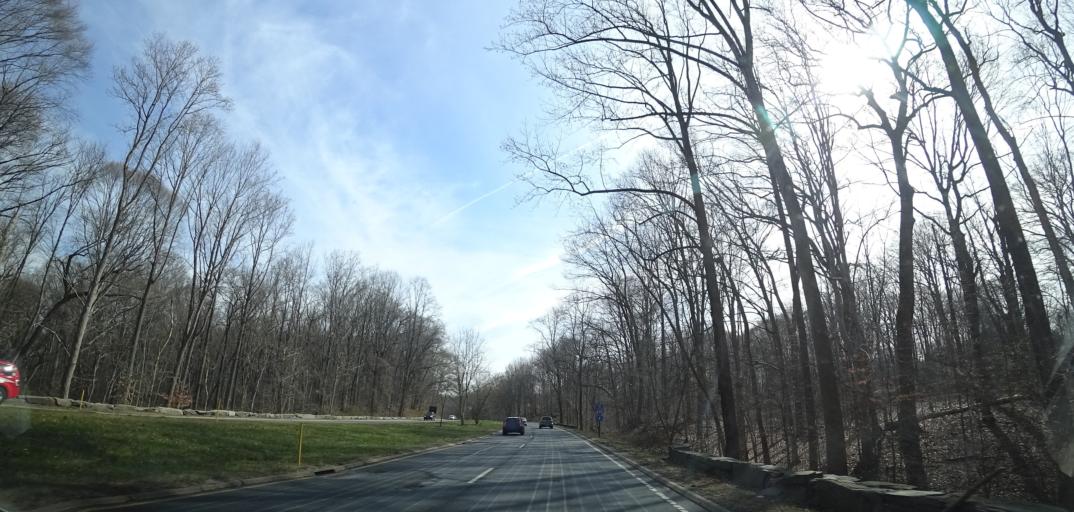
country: US
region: Maryland
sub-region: Montgomery County
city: Cabin John
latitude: 38.9637
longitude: -77.1700
